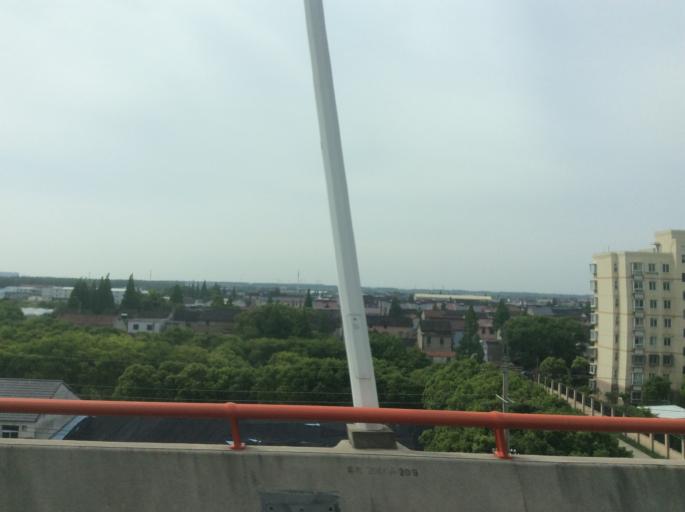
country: CN
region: Shanghai Shi
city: Kangqiao
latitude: 31.2063
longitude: 121.7135
